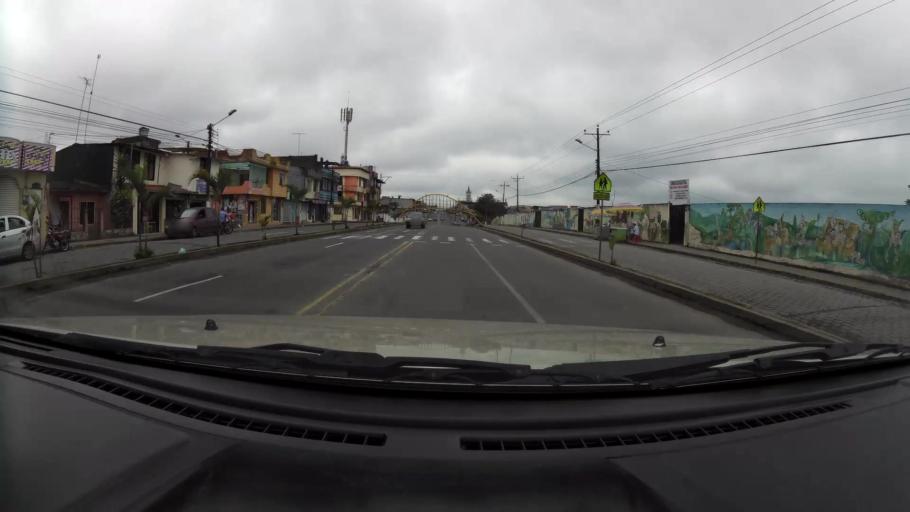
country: EC
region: Santo Domingo de los Tsachilas
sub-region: Canton Santo Domingo de los Colorados
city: Santo Domingo de los Colorados
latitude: -0.2457
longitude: -79.1837
